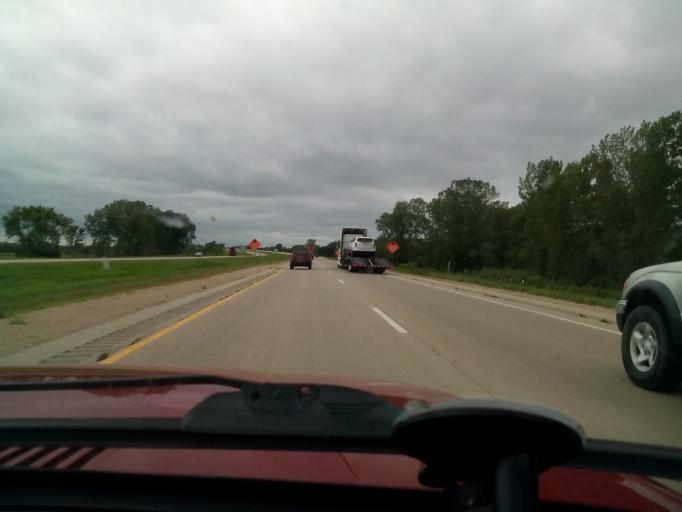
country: US
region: Wisconsin
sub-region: Columbia County
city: Columbus
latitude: 43.3558
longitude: -89.0142
